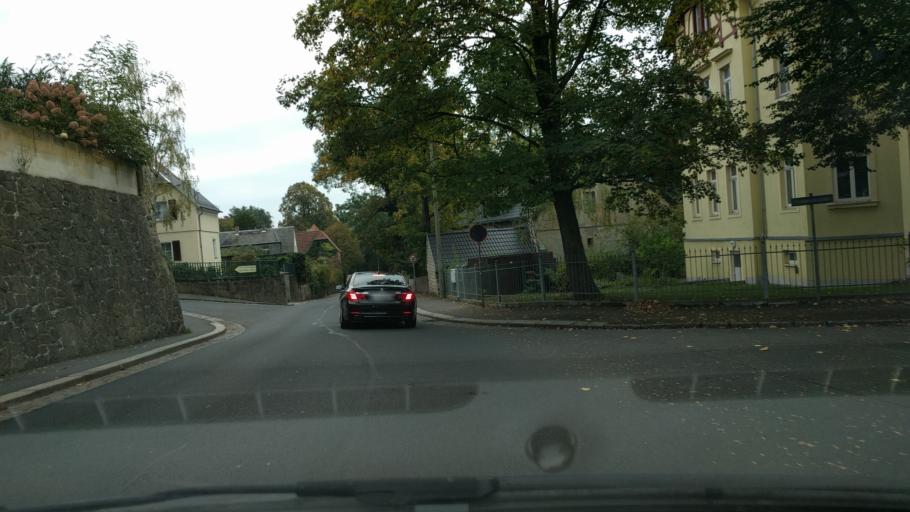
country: DE
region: Saxony
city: Albertstadt
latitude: 51.0628
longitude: 13.8111
